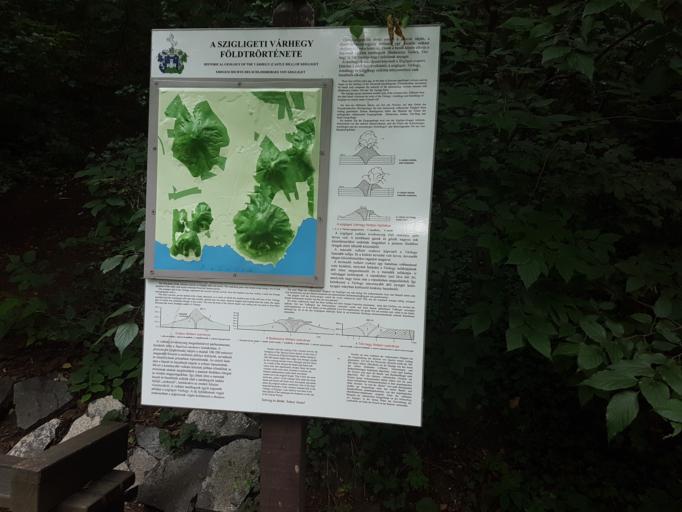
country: HU
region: Veszprem
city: Tapolca
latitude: 46.8039
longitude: 17.4354
